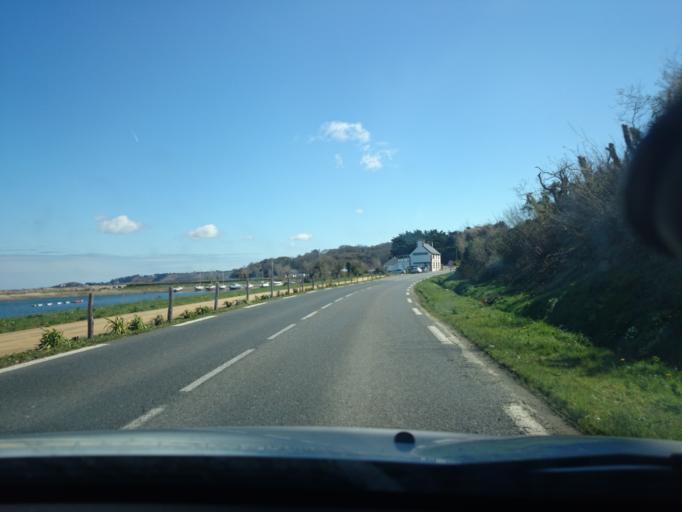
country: FR
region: Brittany
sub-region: Departement des Cotes-d'Armor
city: Perros-Guirec
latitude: 48.7972
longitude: -3.4324
